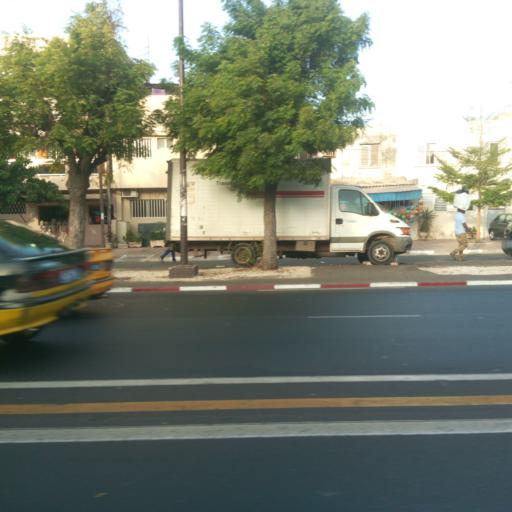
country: SN
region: Dakar
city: Dakar
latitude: 14.6850
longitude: -17.4451
